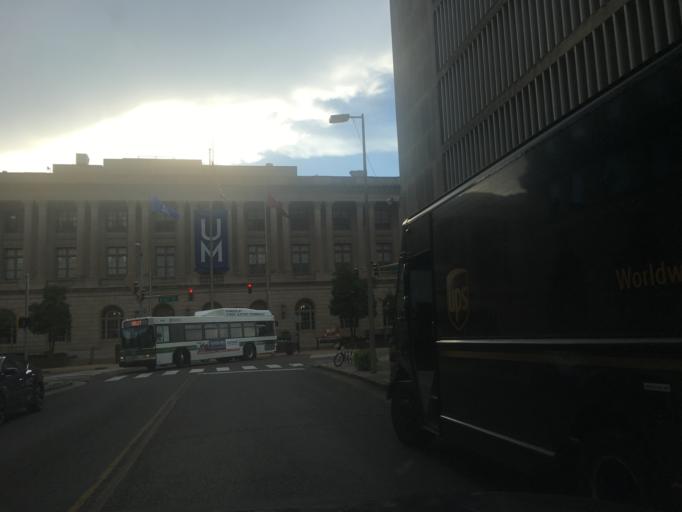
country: US
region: Tennessee
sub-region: Shelby County
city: Memphis
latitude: 35.1454
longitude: -90.0536
